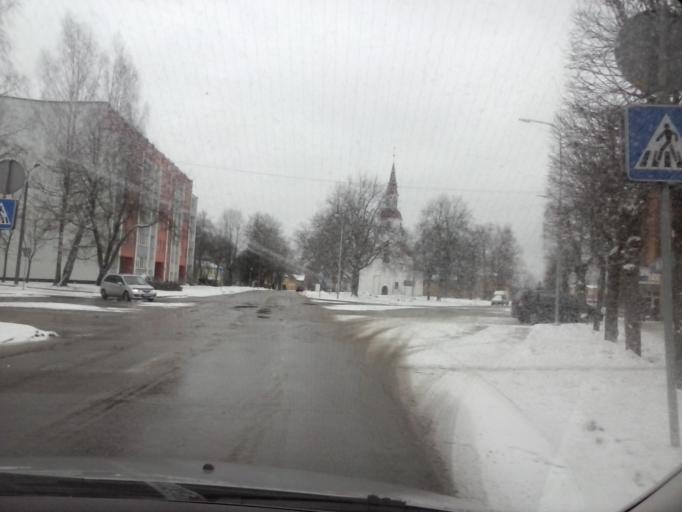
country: LV
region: Valkas Rajons
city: Valka
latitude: 57.7750
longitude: 26.0208
